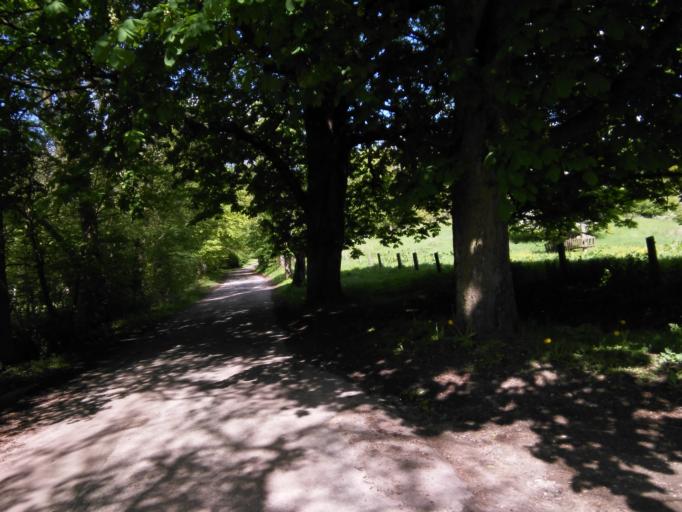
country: DK
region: Central Jutland
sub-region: Arhus Kommune
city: Beder
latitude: 56.0862
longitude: 10.2325
